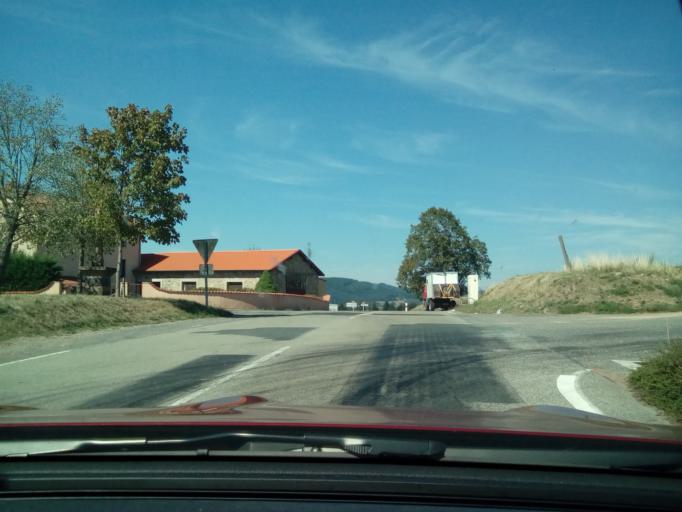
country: FR
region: Rhone-Alpes
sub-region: Departement du Rhone
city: Cublize
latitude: 45.9815
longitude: 4.3743
